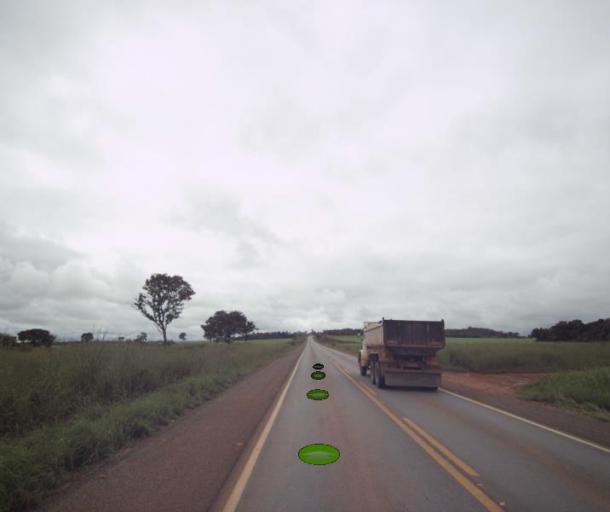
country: BR
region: Goias
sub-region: Uruacu
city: Uruacu
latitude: -14.6702
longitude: -49.1437
